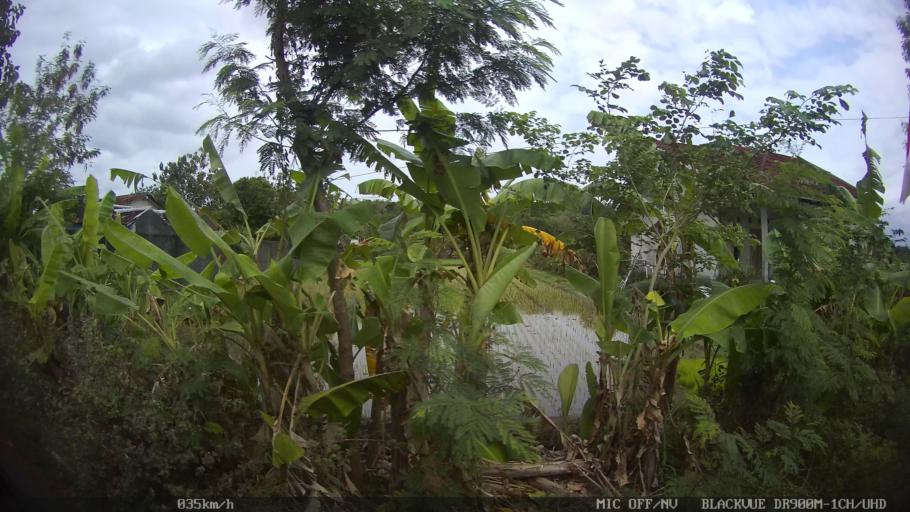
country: ID
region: Daerah Istimewa Yogyakarta
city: Depok
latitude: -7.8245
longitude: 110.4639
